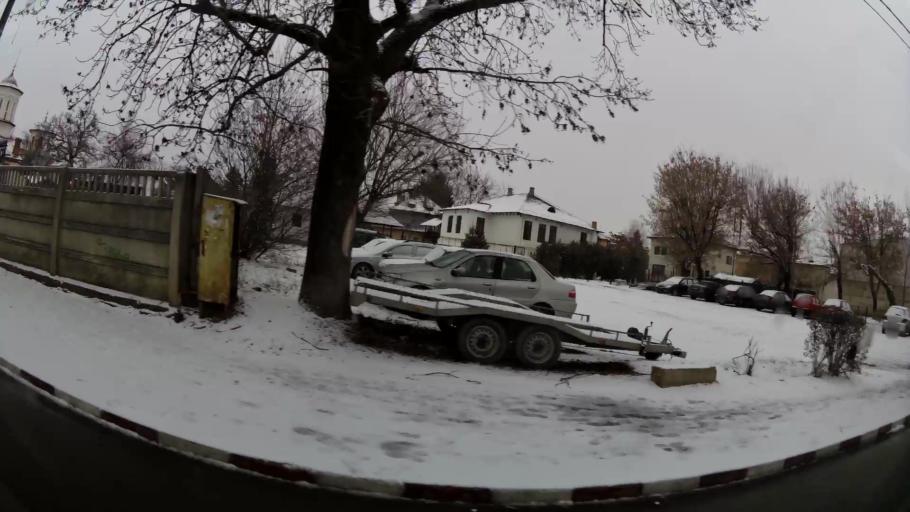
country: RO
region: Dambovita
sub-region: Municipiul Targoviste
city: Targoviste
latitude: 44.9298
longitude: 25.4560
